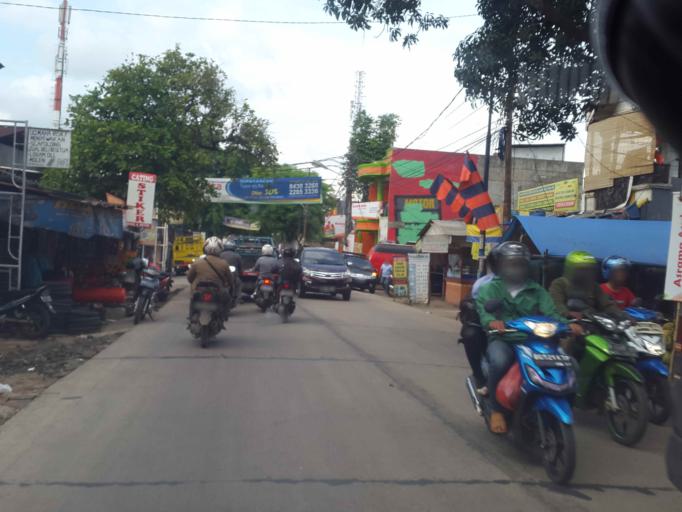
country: ID
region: West Java
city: Cileungsir
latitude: -6.3104
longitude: 106.9244
